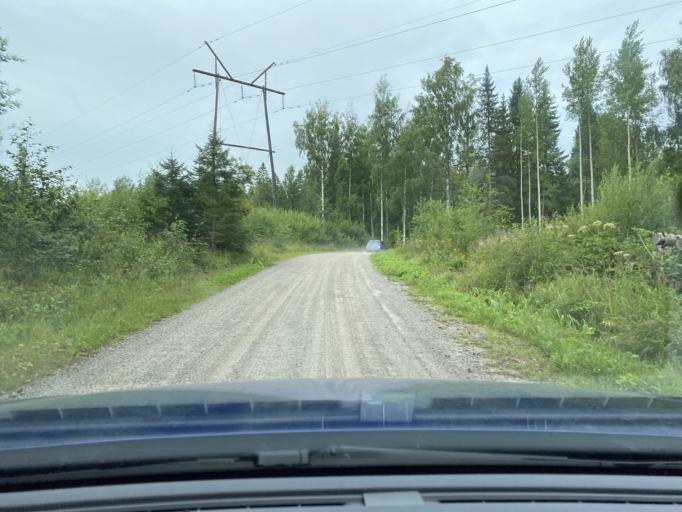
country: FI
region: Pirkanmaa
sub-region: Ylae-Pirkanmaa
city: Maenttae
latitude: 62.0226
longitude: 24.7197
